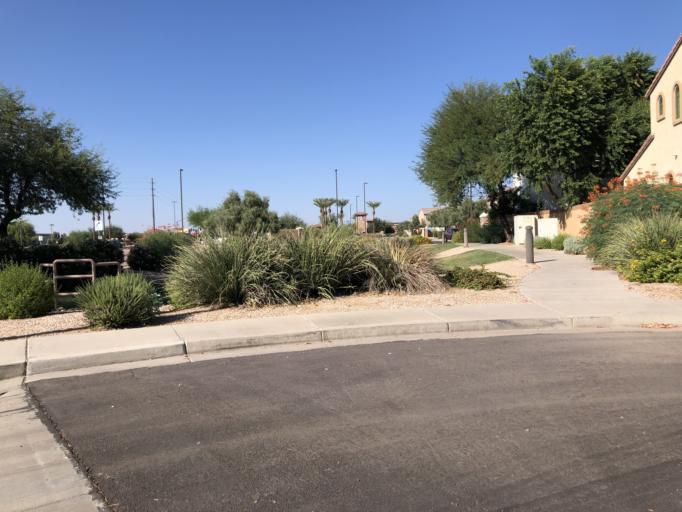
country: US
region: Arizona
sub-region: Maricopa County
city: Queen Creek
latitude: 33.2316
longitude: -111.7201
